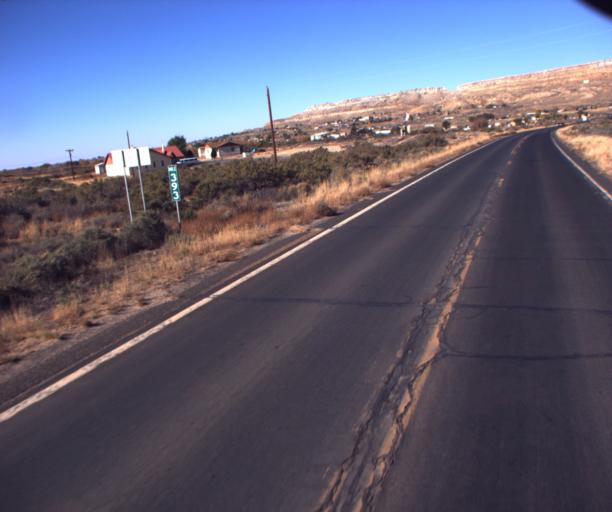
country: US
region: Arizona
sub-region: Navajo County
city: First Mesa
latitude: 35.8398
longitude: -110.3598
